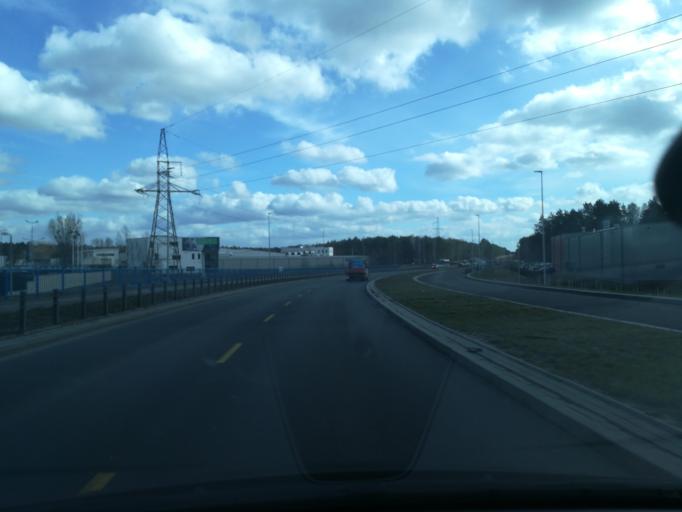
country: PL
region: Kujawsko-Pomorskie
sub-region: Torun
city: Torun
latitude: 52.9911
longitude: 18.6620
